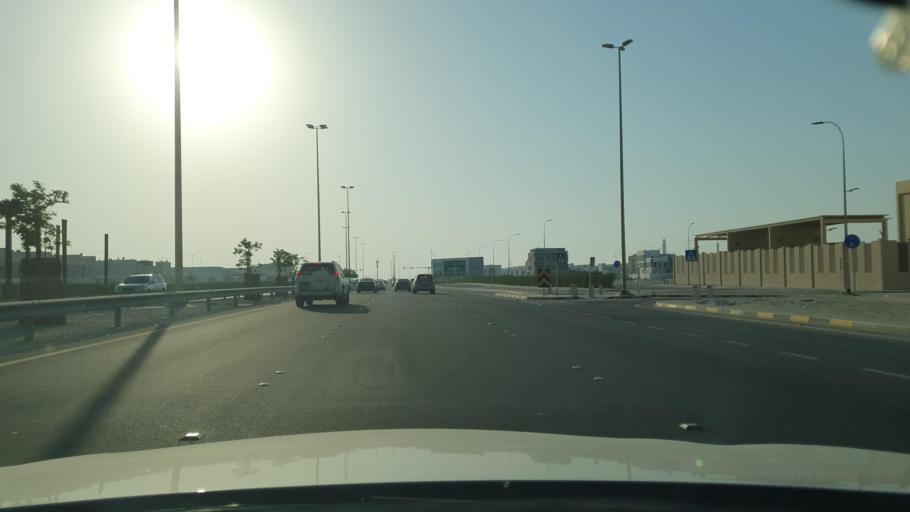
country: BH
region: Muharraq
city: Al Muharraq
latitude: 26.3052
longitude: 50.6320
